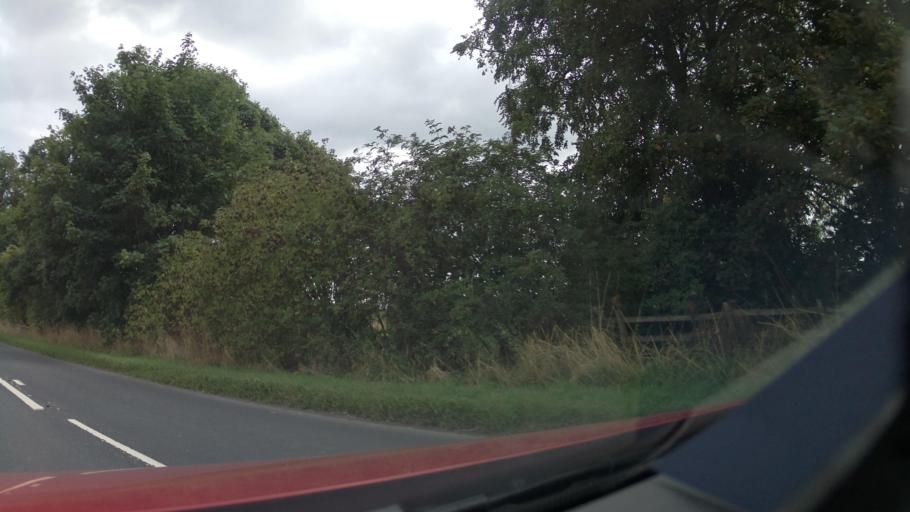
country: GB
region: England
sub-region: North Yorkshire
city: Ripon
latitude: 54.1947
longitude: -1.5742
